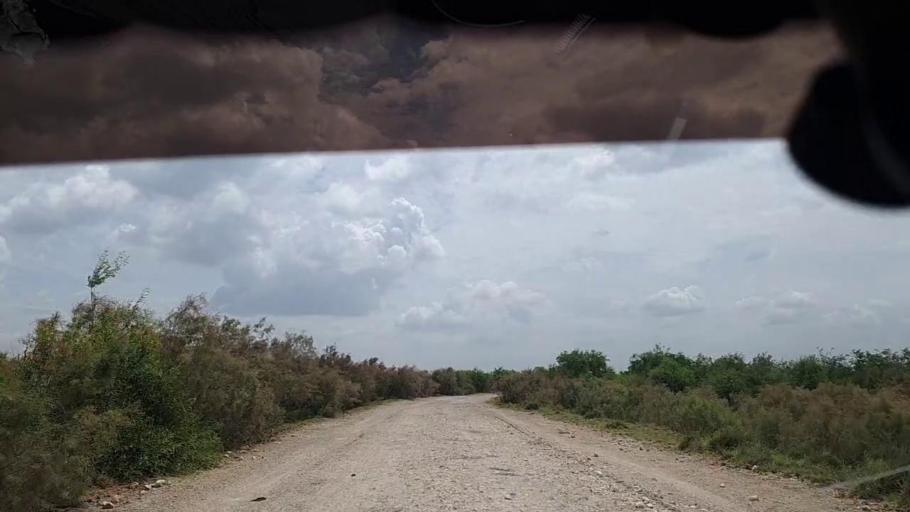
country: PK
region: Sindh
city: Ghauspur
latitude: 28.0629
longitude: 68.9402
